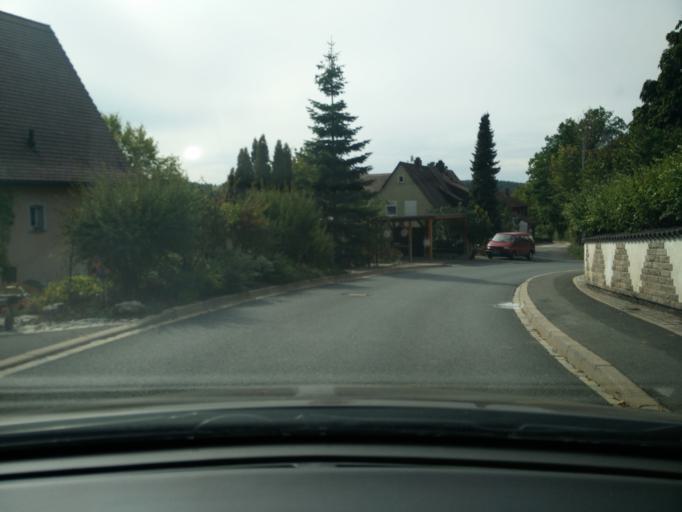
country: DE
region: Bavaria
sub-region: Regierungsbezirk Mittelfranken
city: Puschendorf
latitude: 49.5176
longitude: 10.8091
